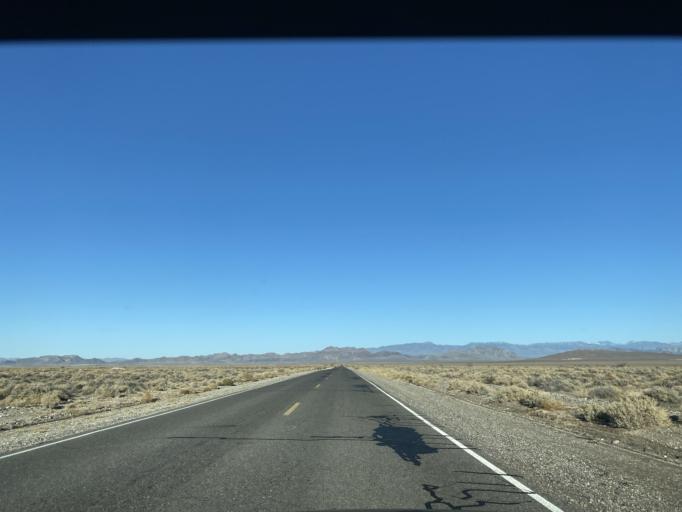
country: US
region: Nevada
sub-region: Nye County
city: Pahrump
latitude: 36.3168
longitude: -116.3853
